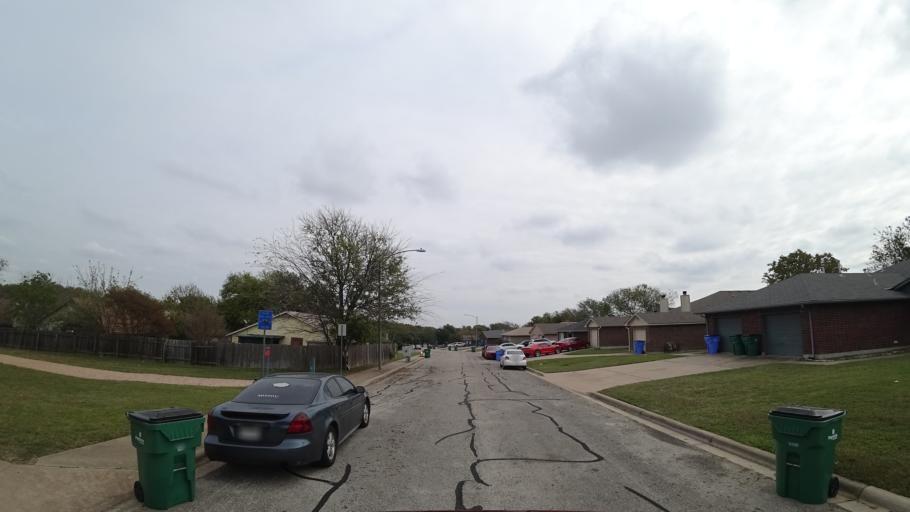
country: US
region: Texas
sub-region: Travis County
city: Wells Branch
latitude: 30.4365
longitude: -97.6808
